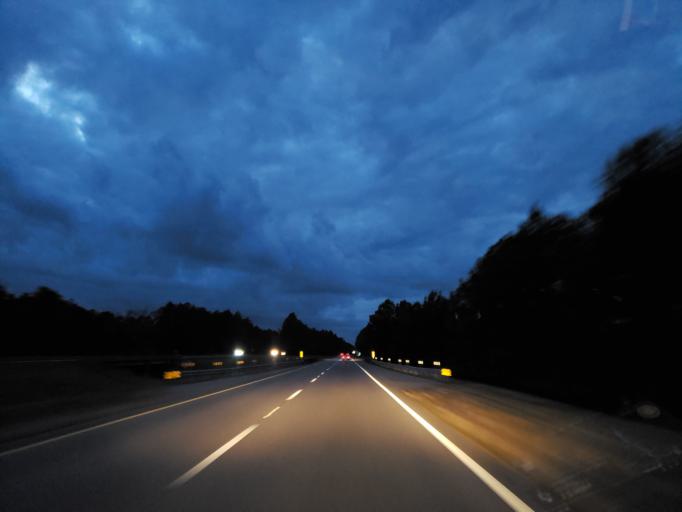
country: US
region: Mississippi
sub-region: Forrest County
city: Hattiesburg
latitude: 31.2454
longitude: -89.2469
